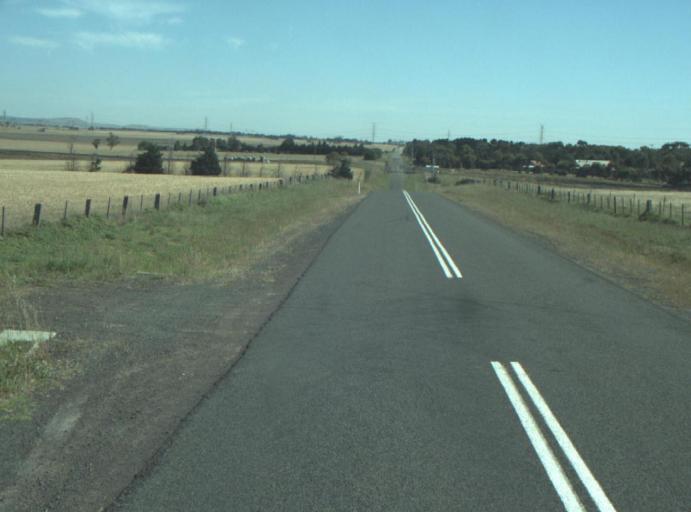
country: AU
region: Victoria
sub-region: Greater Geelong
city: Bell Post Hill
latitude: -38.0808
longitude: 144.3078
